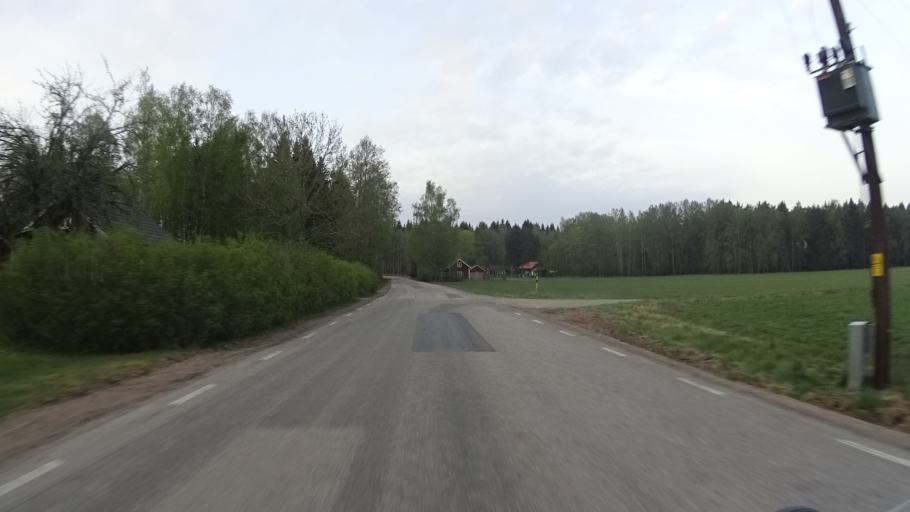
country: SE
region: Vaestra Goetaland
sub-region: Gotene Kommun
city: Kallby
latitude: 58.4875
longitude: 13.3148
